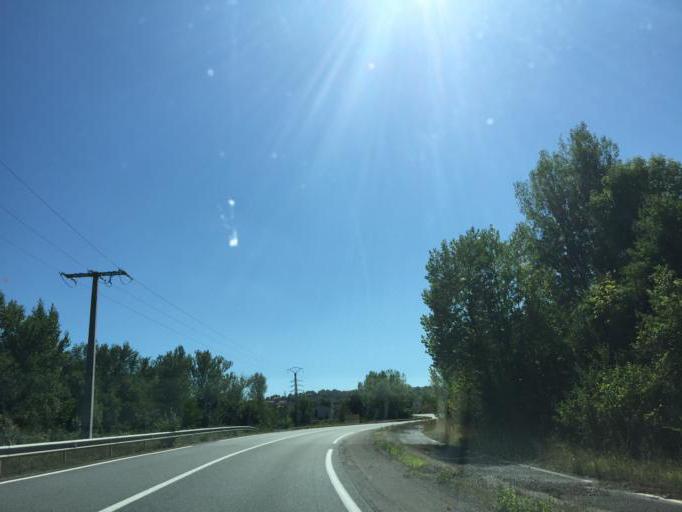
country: FR
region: Midi-Pyrenees
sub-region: Departement de l'Aveyron
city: Saint-Affrique
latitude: 43.9791
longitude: 2.9652
